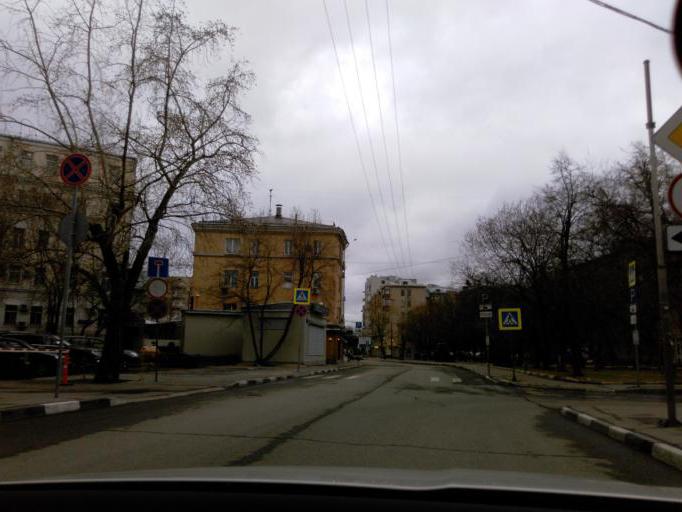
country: RU
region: Moskovskaya
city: Dorogomilovo
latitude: 55.7690
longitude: 37.5861
